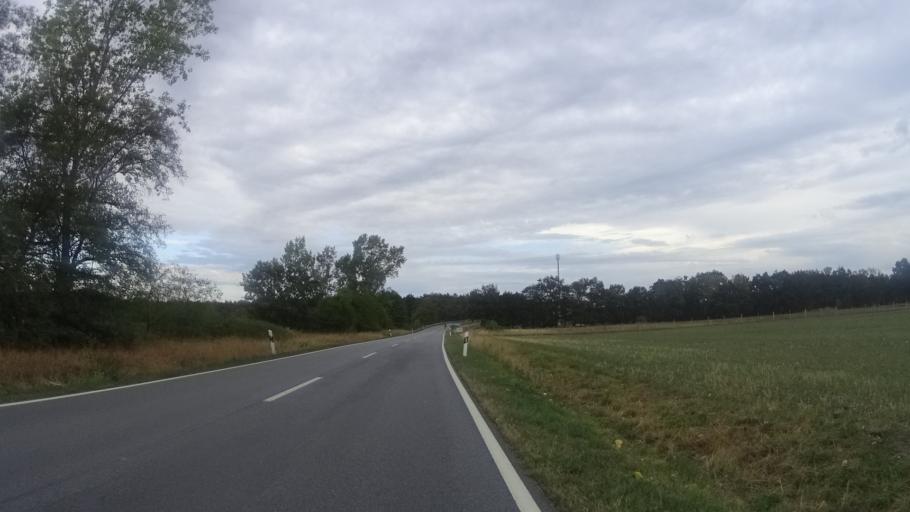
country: PL
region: Lower Silesian Voivodeship
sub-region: Powiat zgorzelecki
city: Piensk
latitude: 51.2832
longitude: 15.0251
